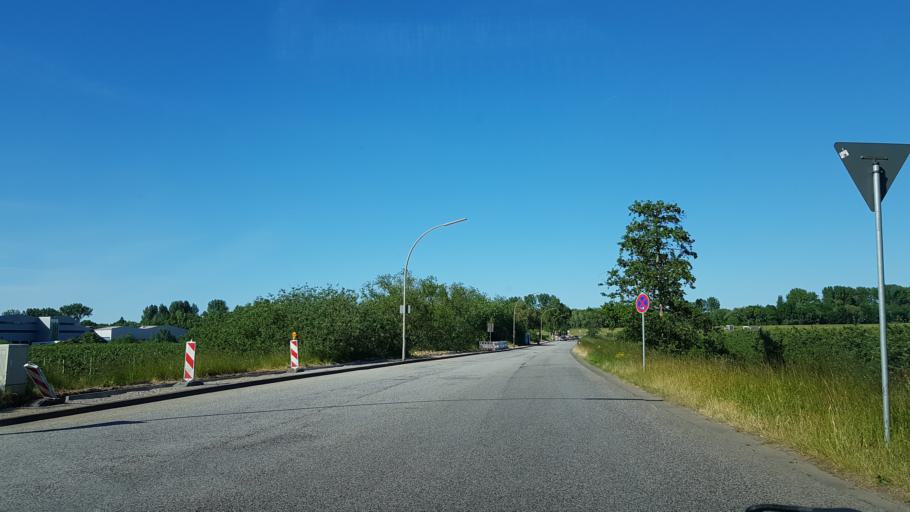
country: DE
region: Lower Saxony
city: Neu Wulmstorf
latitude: 53.5267
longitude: 9.8008
